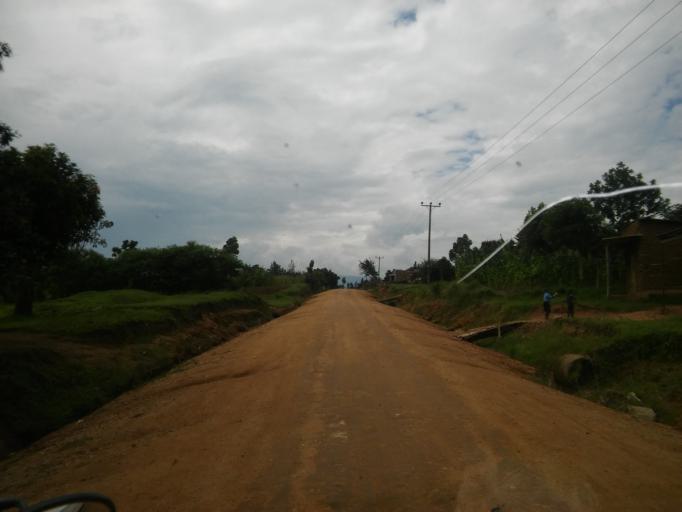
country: KE
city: Malikisi
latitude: 0.8169
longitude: 34.3481
